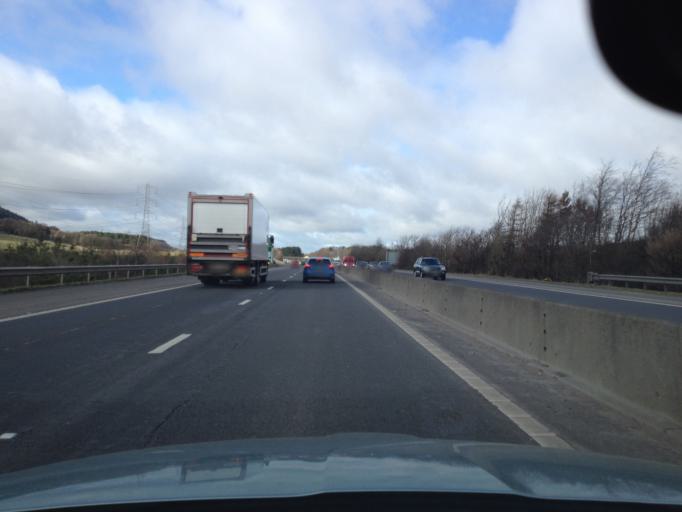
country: GB
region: Scotland
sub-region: Edinburgh
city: Colinton
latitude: 55.8988
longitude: -3.2209
